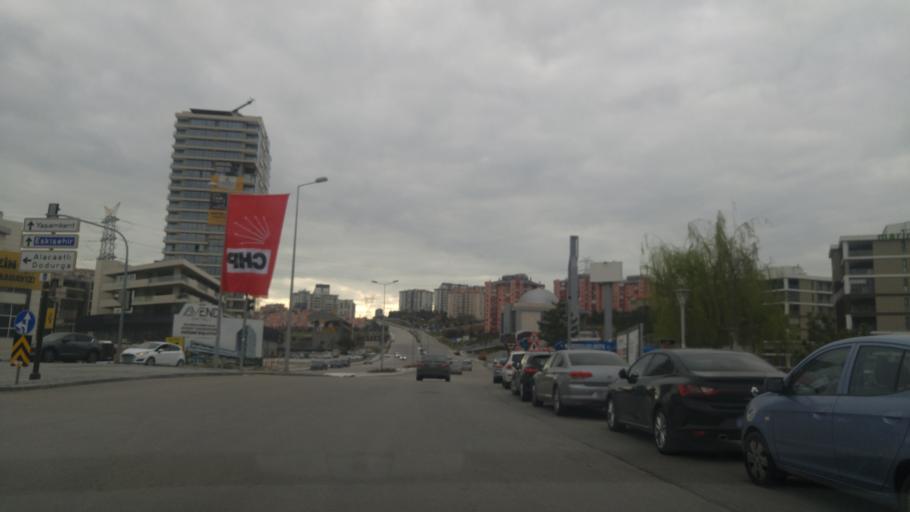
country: TR
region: Ankara
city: Etimesgut
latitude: 39.8606
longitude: 32.6792
